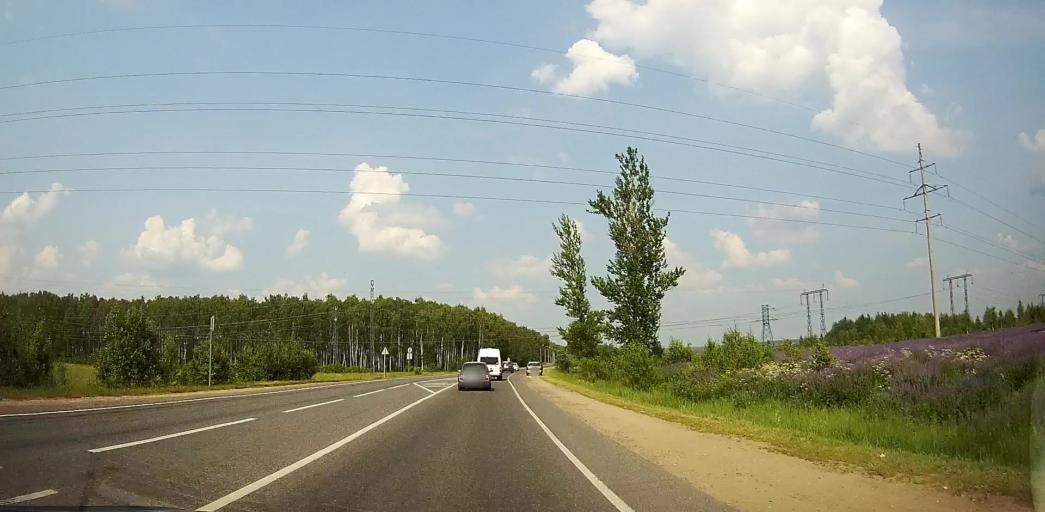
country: RU
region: Moskovskaya
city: Stupino
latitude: 54.9266
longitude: 38.1180
